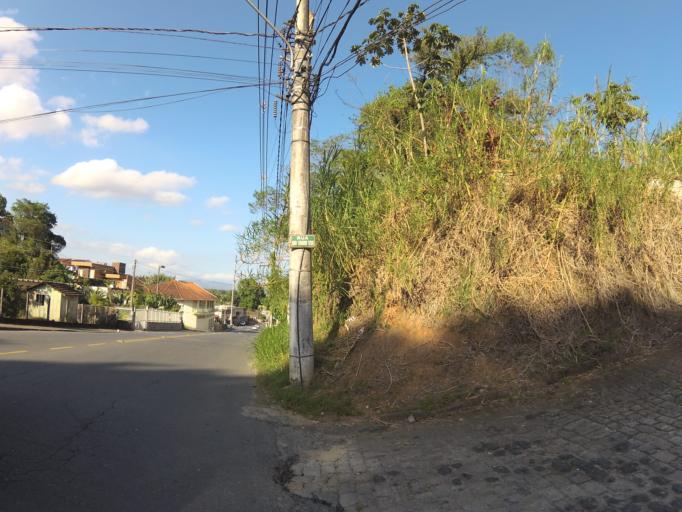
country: BR
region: Santa Catarina
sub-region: Blumenau
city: Blumenau
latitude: -26.9271
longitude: -49.1126
